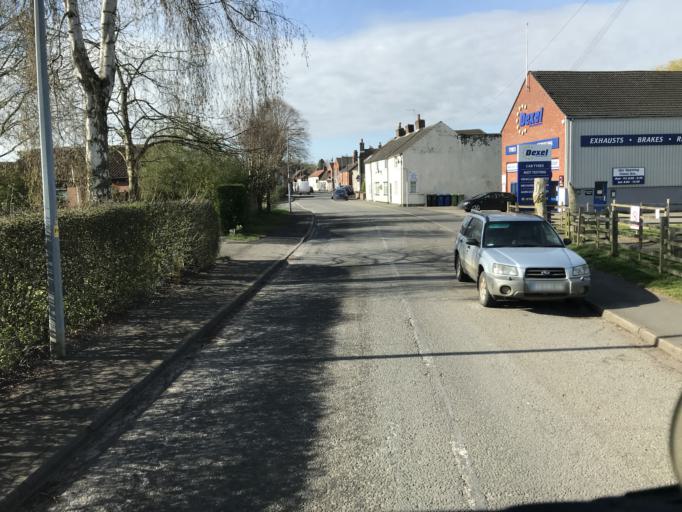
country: GB
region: England
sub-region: Lincolnshire
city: Market Rasen
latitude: 53.3881
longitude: -0.3327
